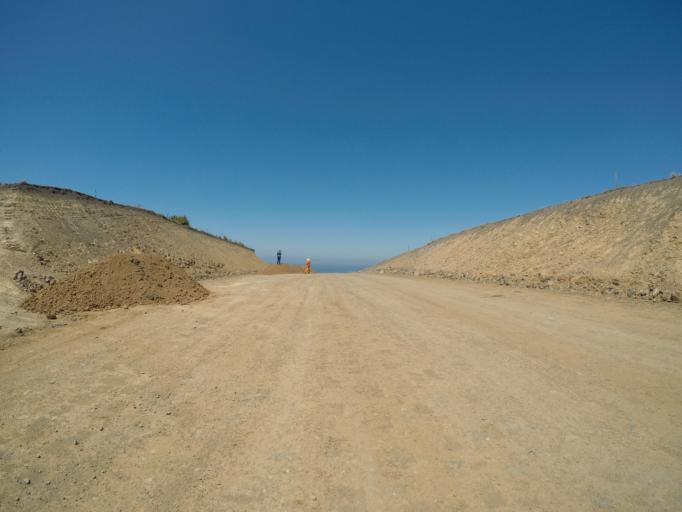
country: ZA
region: Eastern Cape
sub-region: OR Tambo District Municipality
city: Libode
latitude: -32.0229
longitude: 29.1144
